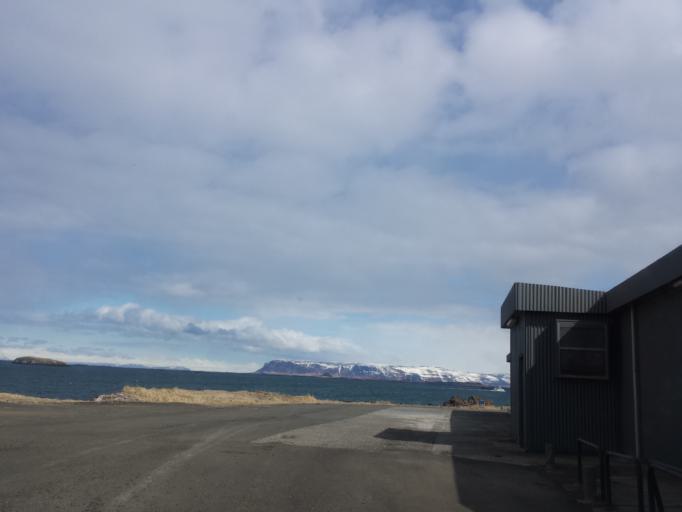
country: IS
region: West
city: Stykkisholmur
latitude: 65.0773
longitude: -22.7205
